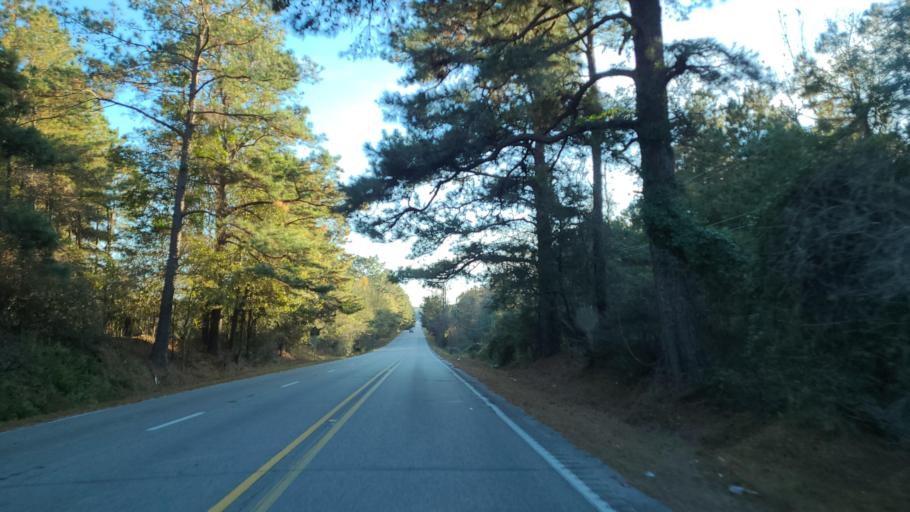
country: US
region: Mississippi
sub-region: Lamar County
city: Purvis
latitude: 31.0960
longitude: -89.4143
